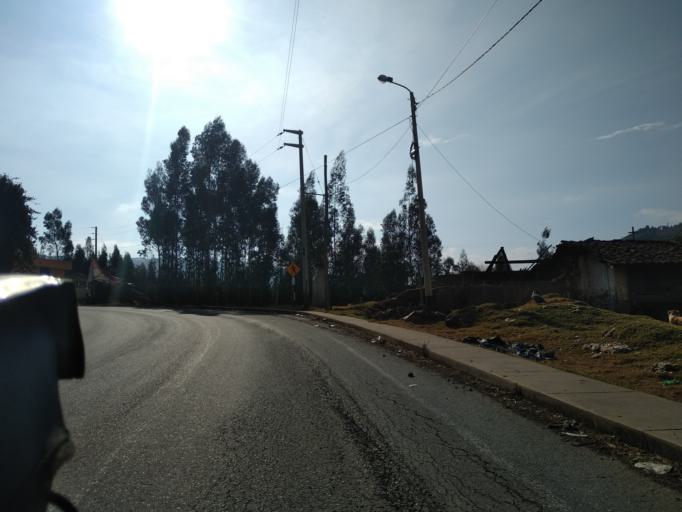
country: PE
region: La Libertad
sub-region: Provincia de Otuzco
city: Agallpampa
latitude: -7.9945
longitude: -78.5159
